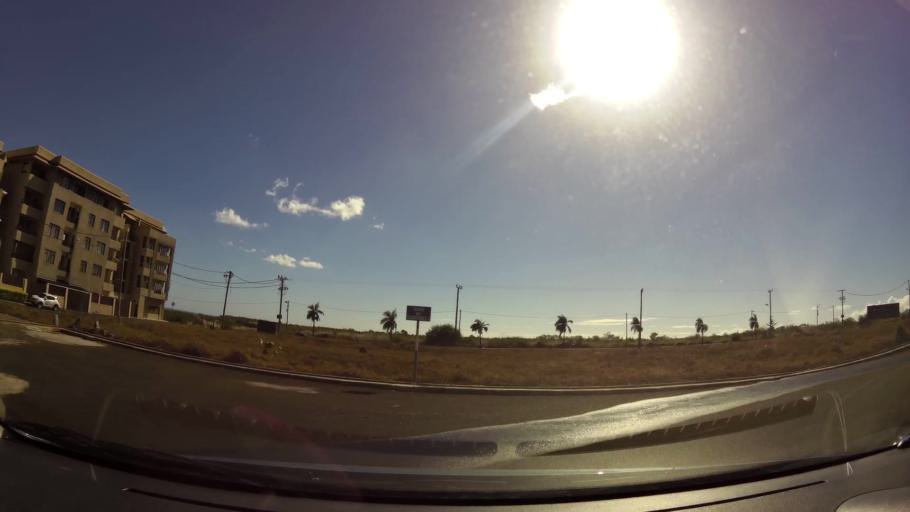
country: MU
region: Black River
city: Flic en Flac
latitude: -20.2772
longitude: 57.3794
